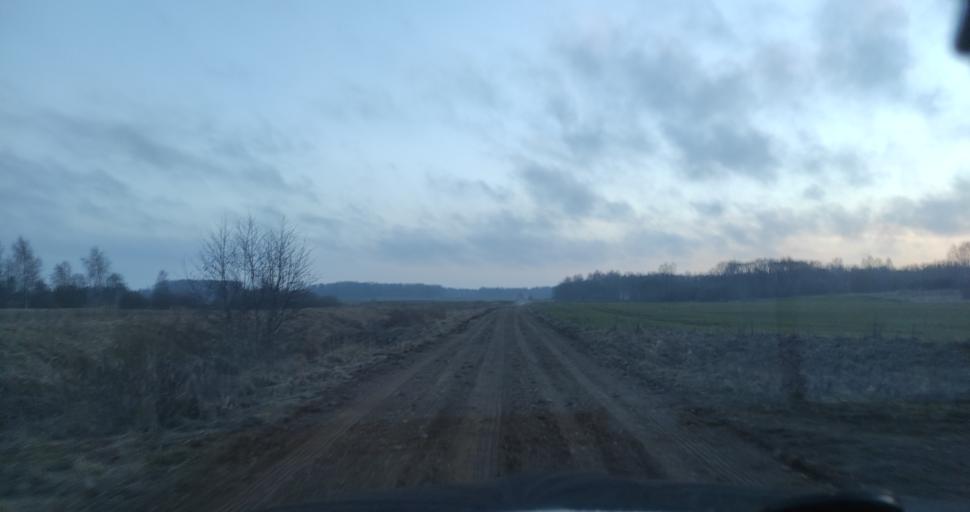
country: LV
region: Aizpute
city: Aizpute
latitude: 56.8138
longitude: 21.7852
